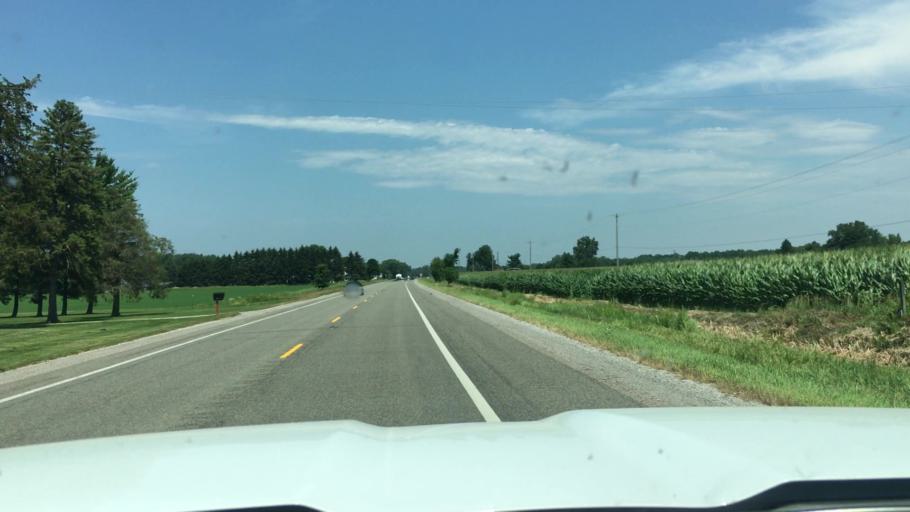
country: US
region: Michigan
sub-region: Saginaw County
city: Chesaning
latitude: 43.1964
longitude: -84.1693
